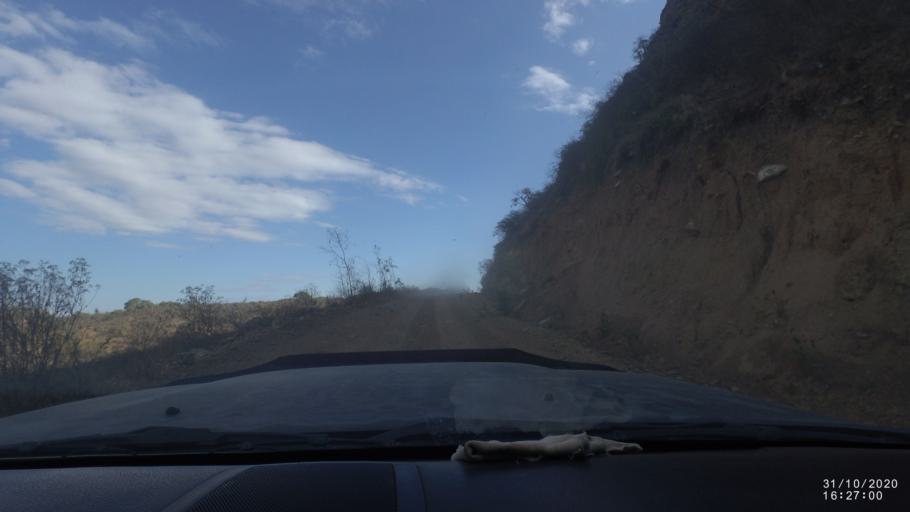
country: BO
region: Chuquisaca
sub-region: Provincia Zudanez
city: Mojocoya
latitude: -18.4031
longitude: -64.5857
